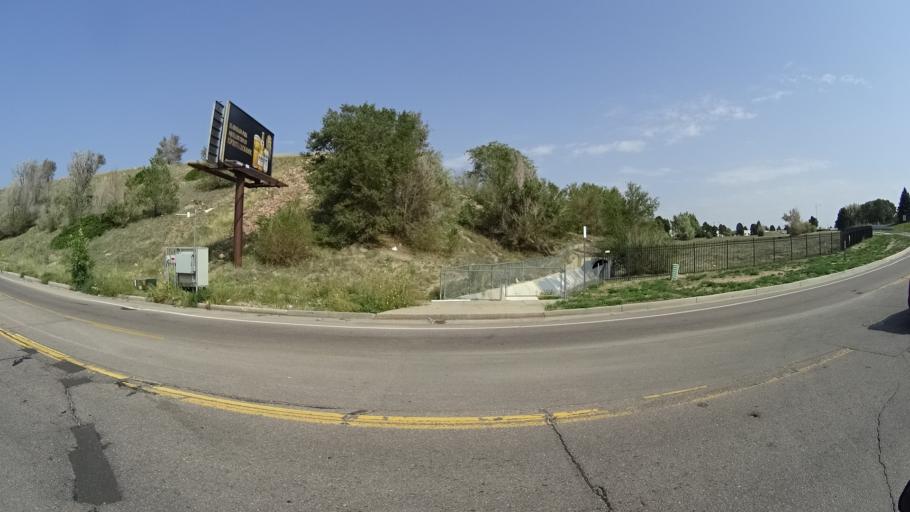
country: US
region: Colorado
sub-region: El Paso County
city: Cimarron Hills
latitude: 38.8355
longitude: -104.7542
